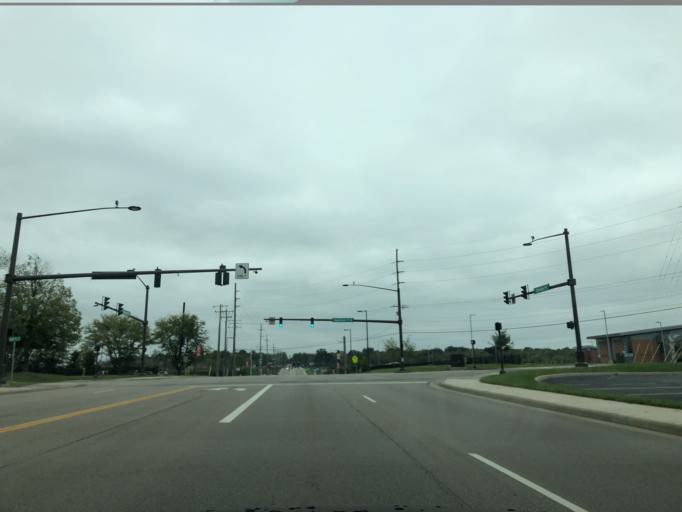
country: US
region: Ohio
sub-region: Hamilton County
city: Glendale
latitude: 39.2775
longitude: -84.4438
